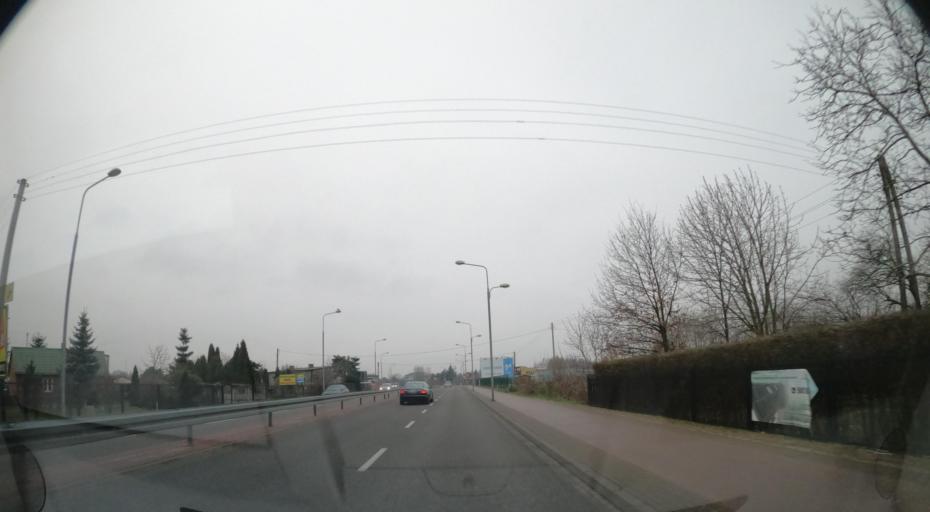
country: PL
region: Masovian Voivodeship
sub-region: Radom
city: Radom
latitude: 51.4213
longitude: 21.2118
